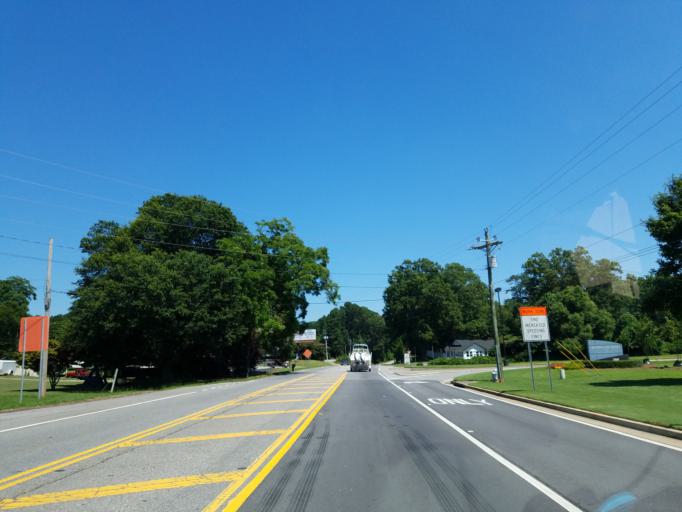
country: US
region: Georgia
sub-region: Forsyth County
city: Cumming
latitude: 34.2624
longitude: -84.0834
